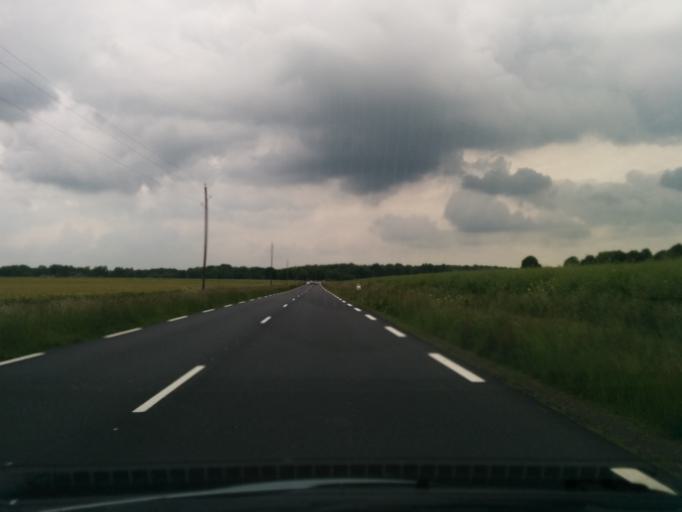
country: FR
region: Ile-de-France
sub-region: Departement des Yvelines
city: Limetz-Villez
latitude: 49.1393
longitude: 1.5281
